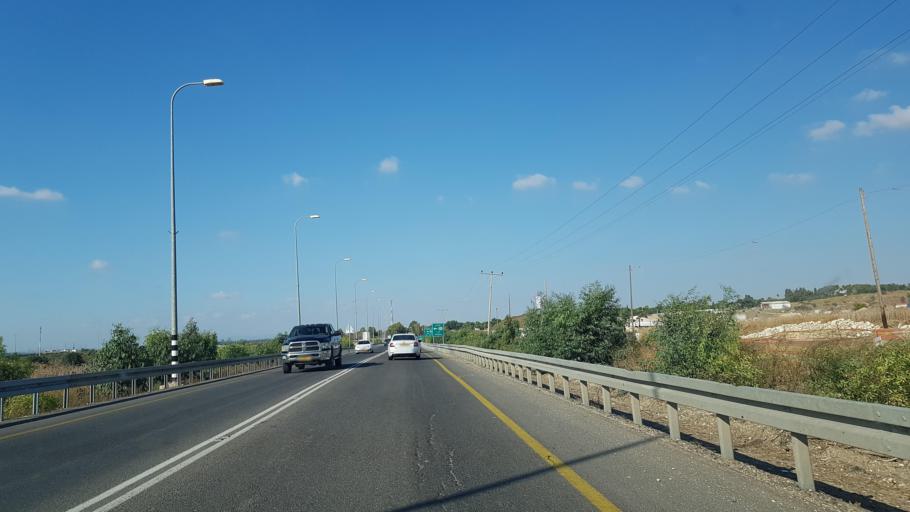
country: PS
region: West Bank
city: Tulkarm
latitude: 32.3415
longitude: 35.0105
